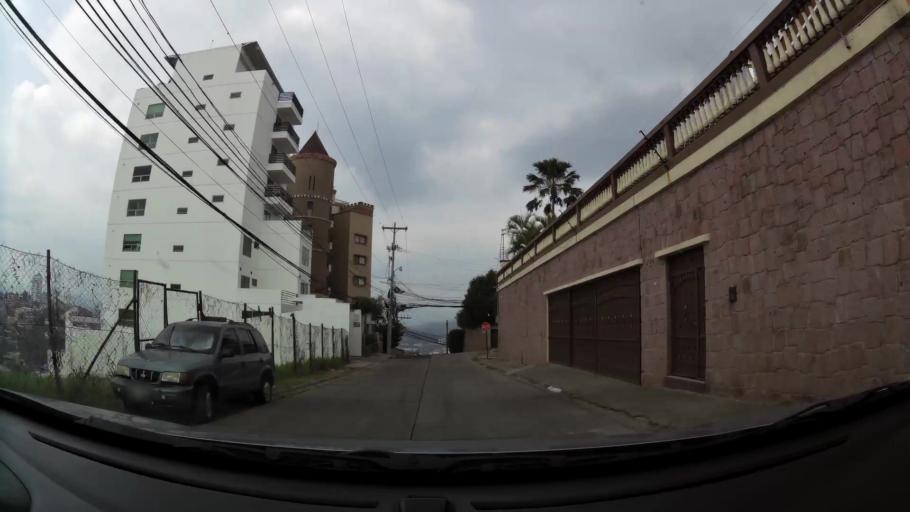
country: HN
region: Francisco Morazan
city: Tegucigalpa
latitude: 14.0912
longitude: -87.1883
